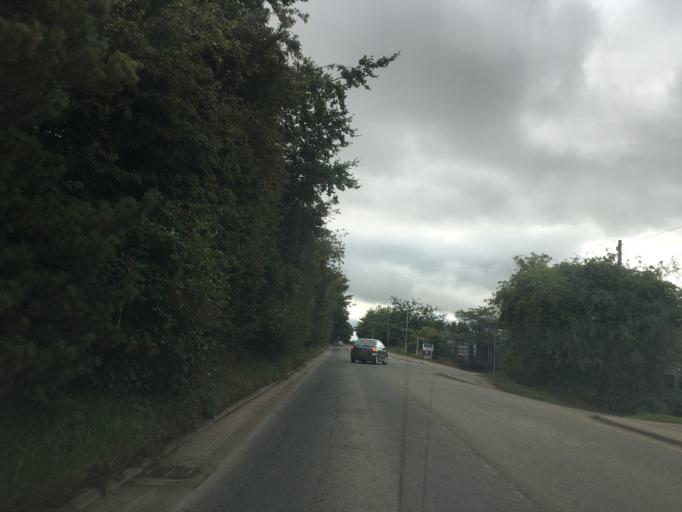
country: GB
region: Scotland
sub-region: Midlothian
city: Gorebridge
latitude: 55.8677
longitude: -3.0529
